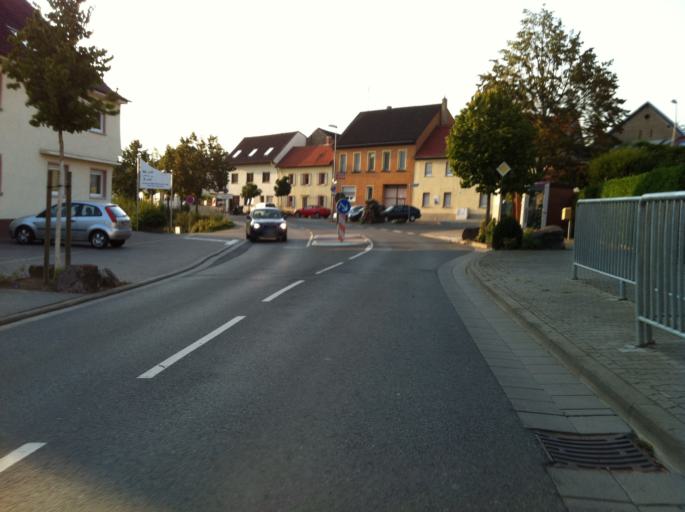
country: DE
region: Rheinland-Pfalz
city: Schwabenheim
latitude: 49.9434
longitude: 8.0804
